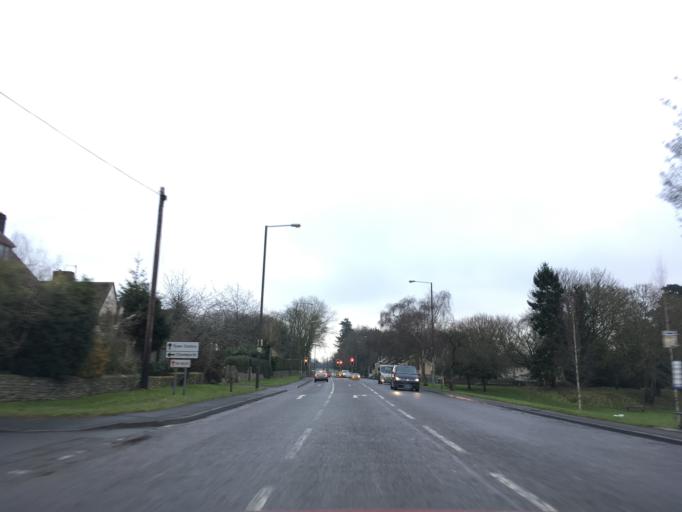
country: GB
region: England
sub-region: Gloucestershire
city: Cirencester
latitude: 51.7222
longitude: -1.9698
